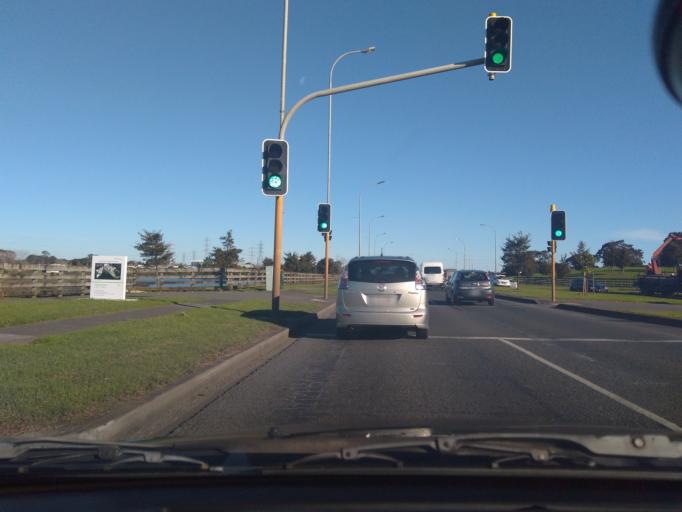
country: NZ
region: Auckland
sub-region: Auckland
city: Manukau City
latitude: -36.9427
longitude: 174.8628
